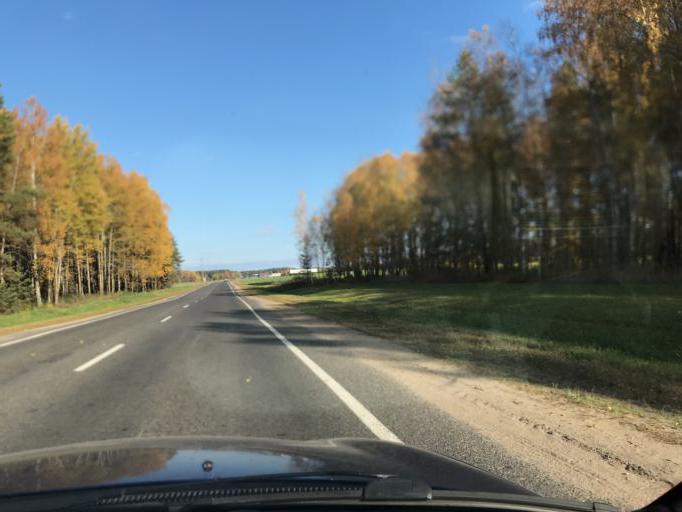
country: BY
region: Grodnenskaya
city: Lida
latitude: 53.9466
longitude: 25.2462
